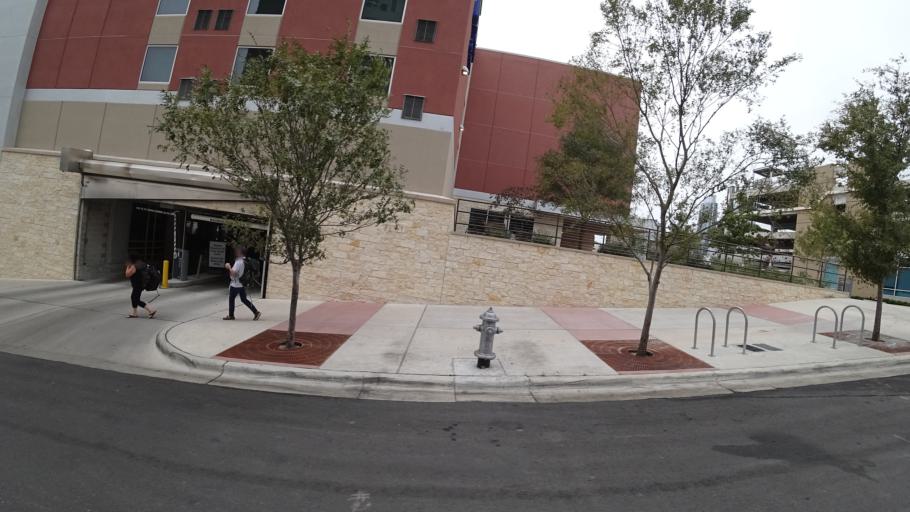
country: US
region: Texas
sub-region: Travis County
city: Austin
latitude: 30.2695
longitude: -97.7370
